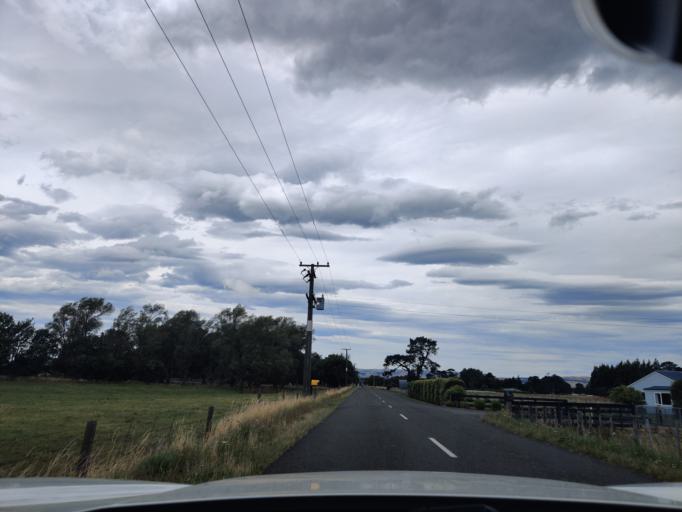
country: NZ
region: Wellington
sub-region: Masterton District
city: Masterton
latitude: -41.0231
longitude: 175.4729
